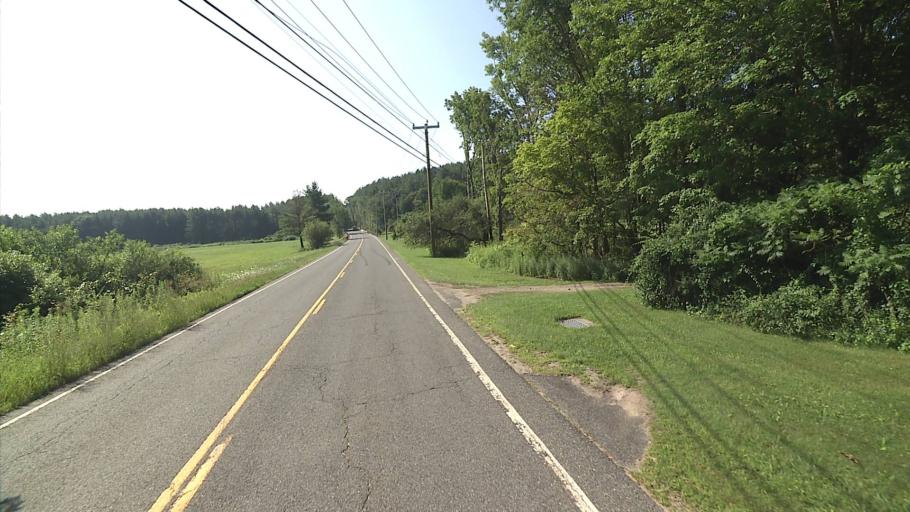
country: US
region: Connecticut
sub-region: Litchfield County
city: Winsted
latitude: 42.0166
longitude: -73.1142
